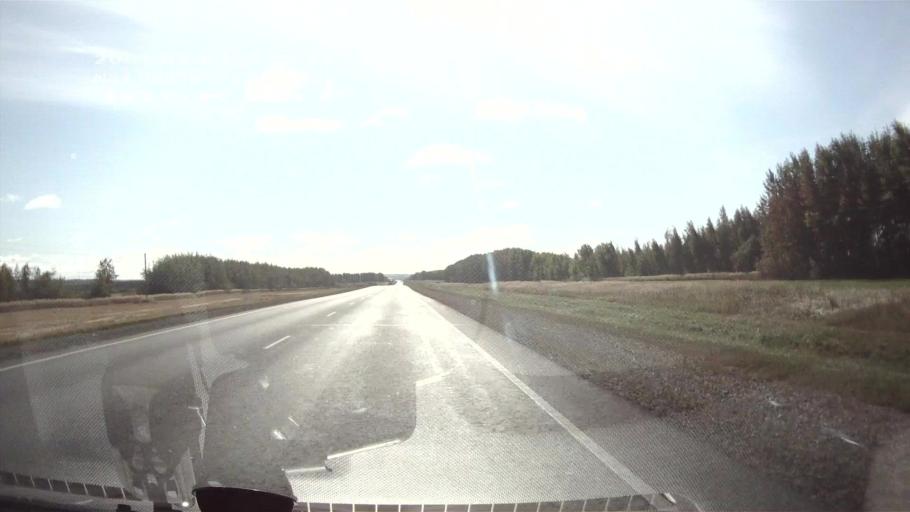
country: RU
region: Ulyanovsk
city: Tsil'na
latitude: 54.5605
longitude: 47.9261
